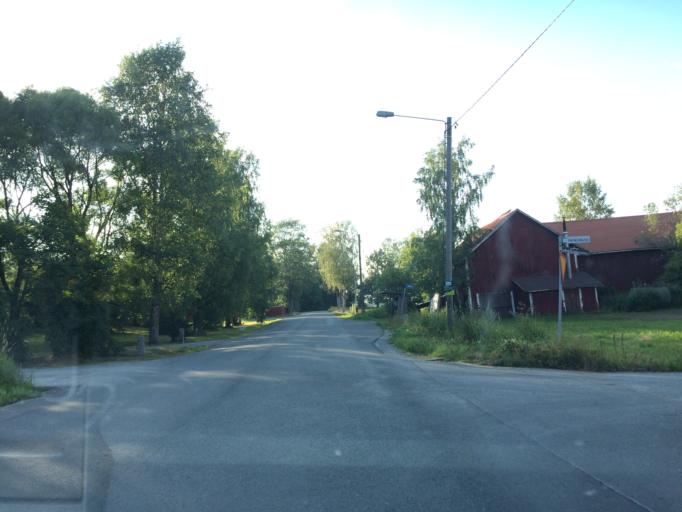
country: FI
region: Haeme
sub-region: Haemeenlinna
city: Parola
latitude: 61.0375
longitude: 24.4023
